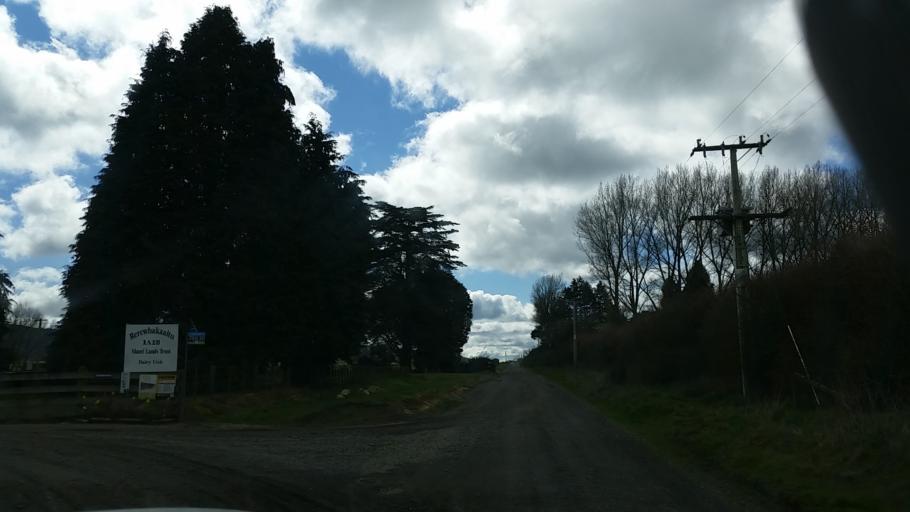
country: NZ
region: Bay of Plenty
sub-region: Whakatane District
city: Murupara
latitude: -38.2847
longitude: 176.5499
